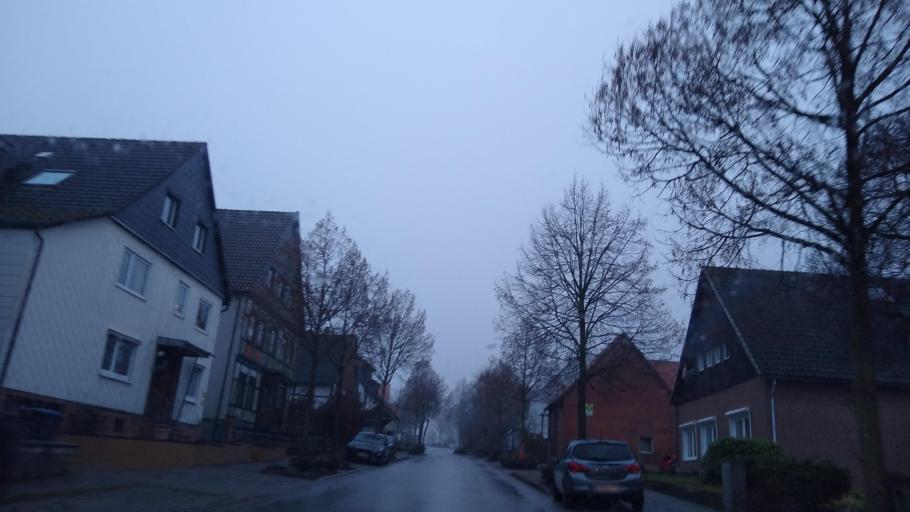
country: DE
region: Lower Saxony
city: Ottenstein
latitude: 51.9462
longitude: 9.4048
